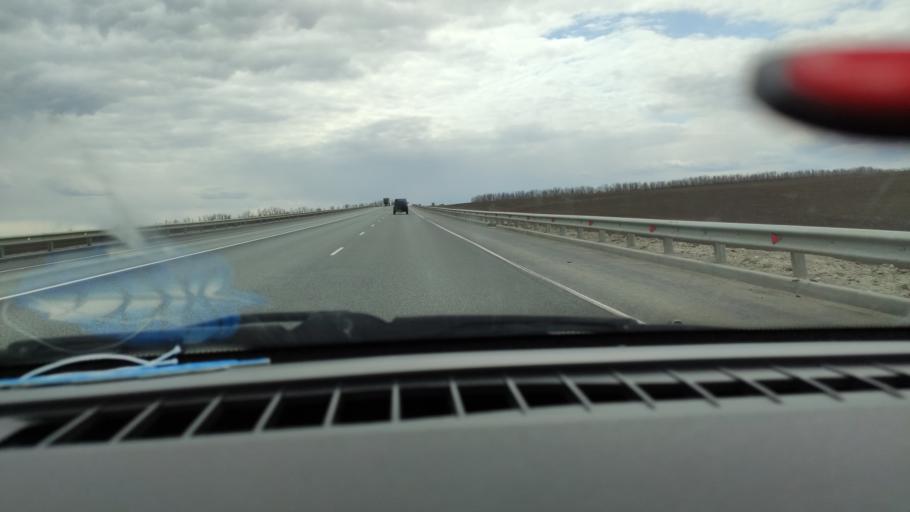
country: RU
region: Saratov
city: Yelshanka
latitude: 51.8356
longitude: 46.4709
